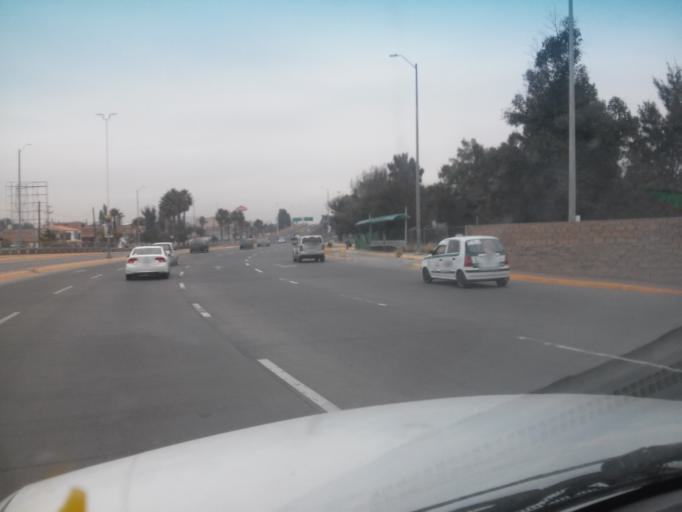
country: MX
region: Durango
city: Victoria de Durango
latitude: 24.0269
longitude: -104.6902
